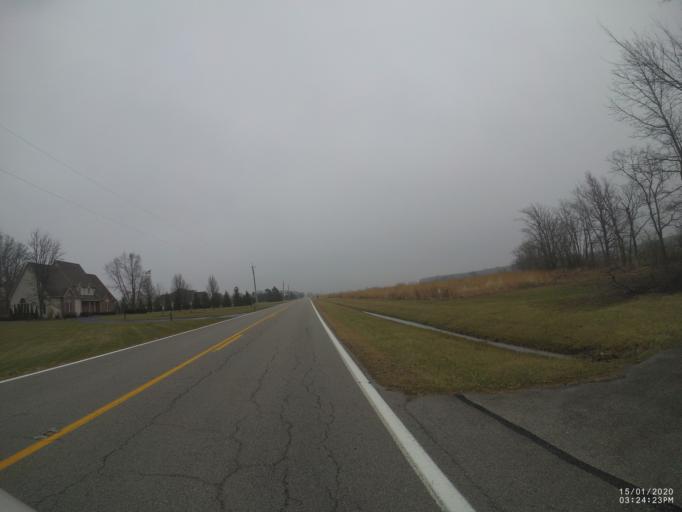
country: US
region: Ohio
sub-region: Sandusky County
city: Woodville
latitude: 41.4282
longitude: -83.4079
